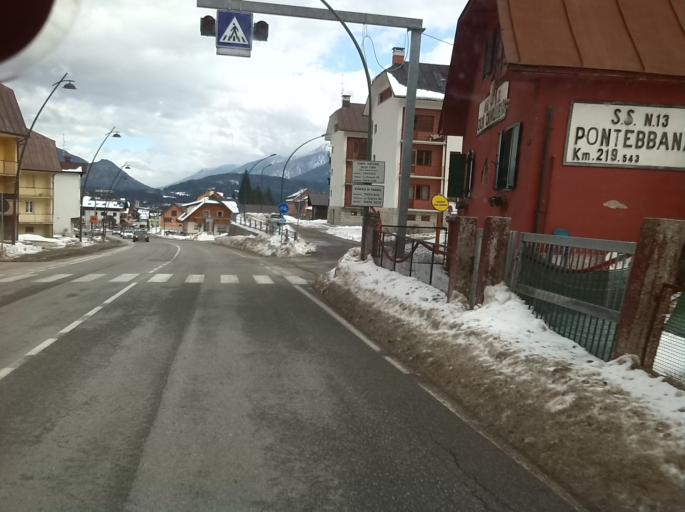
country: IT
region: Friuli Venezia Giulia
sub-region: Provincia di Udine
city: Tarvisio
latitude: 46.5065
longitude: 13.5604
